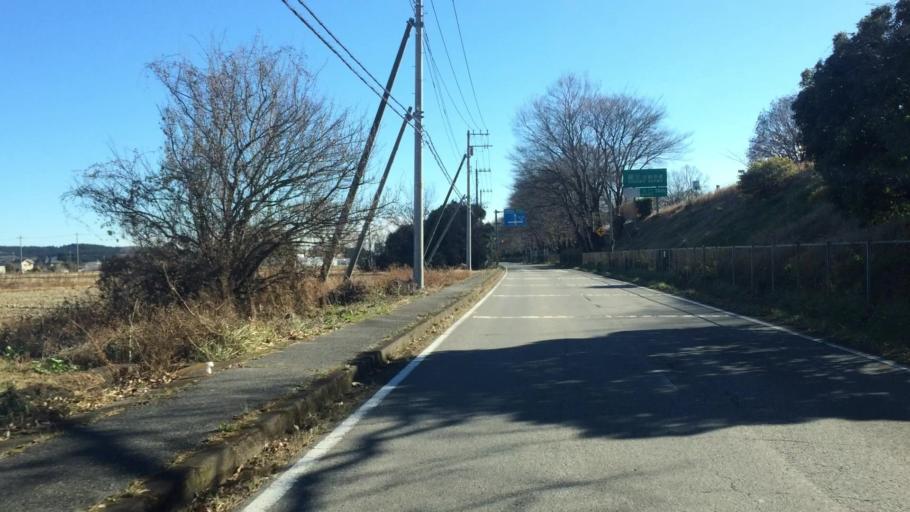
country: JP
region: Tochigi
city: Utsunomiya-shi
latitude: 36.6458
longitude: 139.8397
